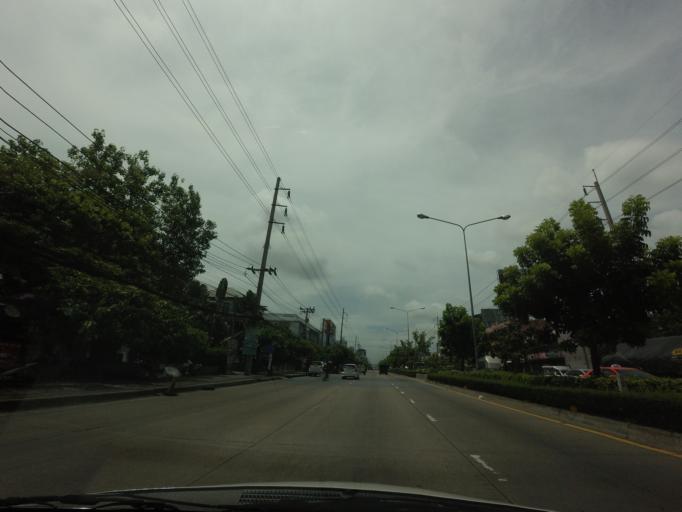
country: TH
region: Samut Prakan
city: Phra Pradaeng
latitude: 13.6530
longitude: 100.5214
